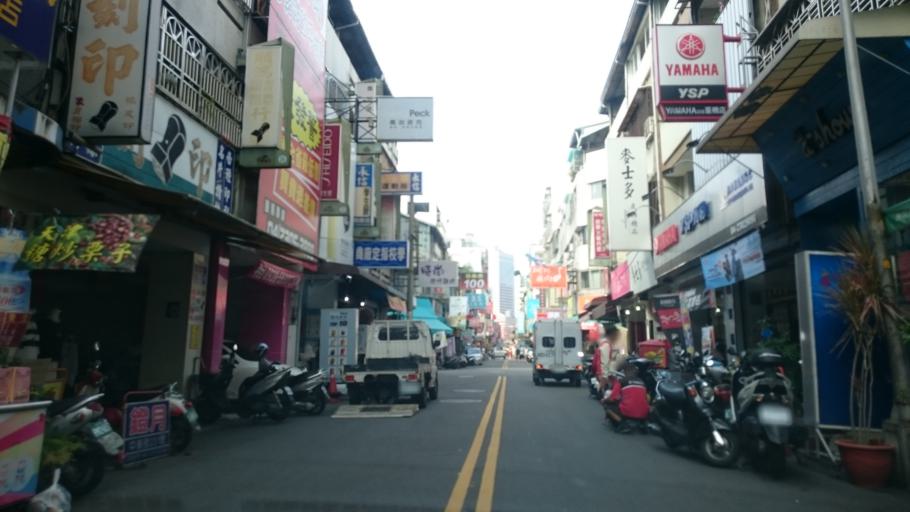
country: TW
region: Taiwan
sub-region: Taichung City
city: Taichung
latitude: 24.1480
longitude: 120.6604
